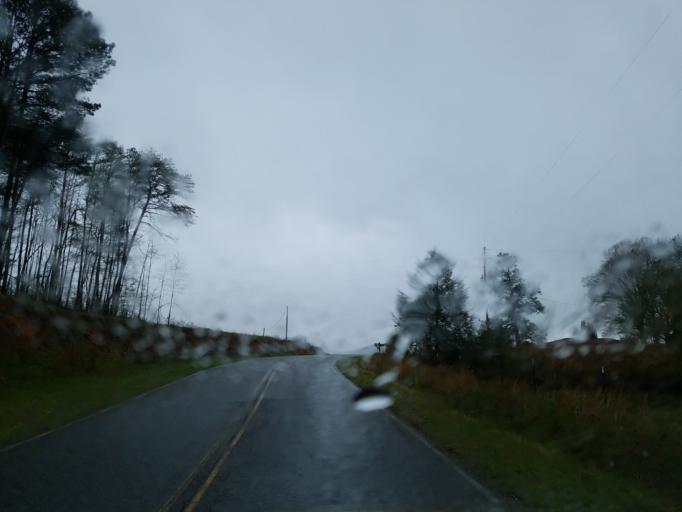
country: US
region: Georgia
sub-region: Fannin County
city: Blue Ridge
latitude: 34.8487
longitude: -84.2299
